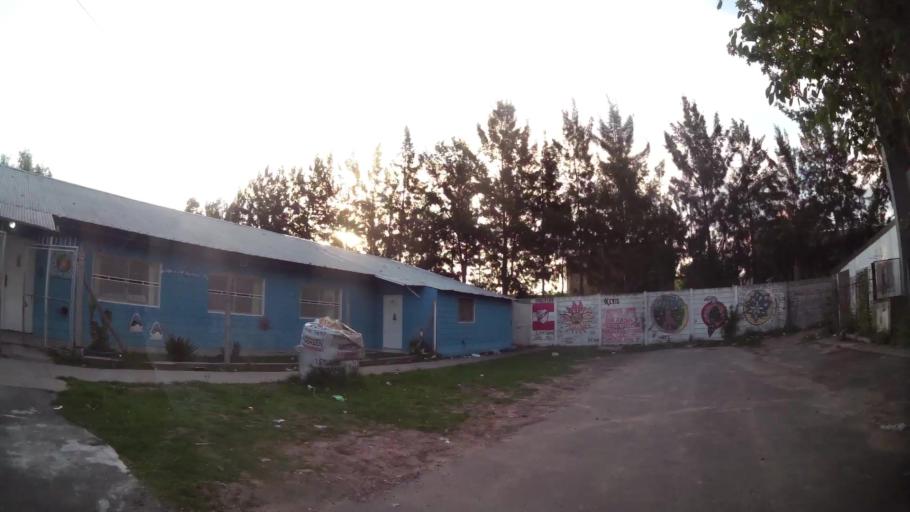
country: AR
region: Buenos Aires
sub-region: Partido de Tigre
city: Tigre
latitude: -34.4491
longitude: -58.6553
